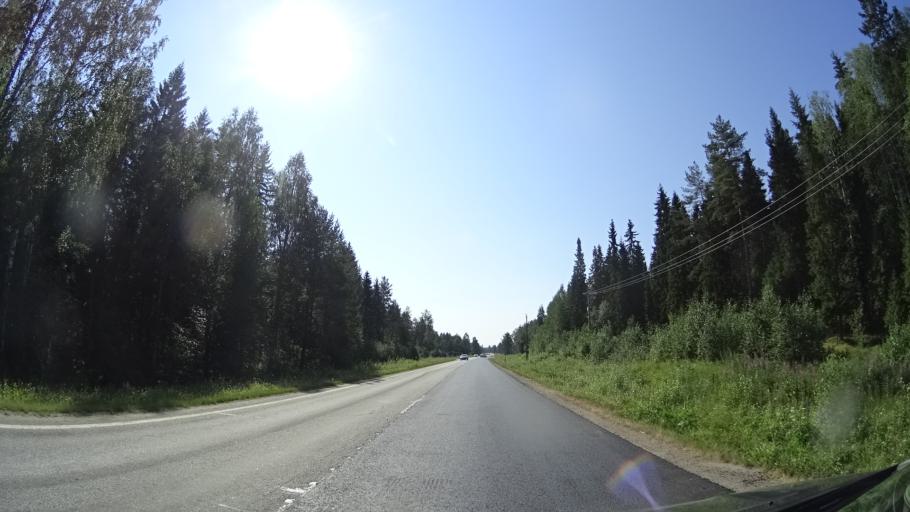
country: FI
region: North Karelia
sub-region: Joensuu
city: Juuka
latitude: 63.2189
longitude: 29.3003
